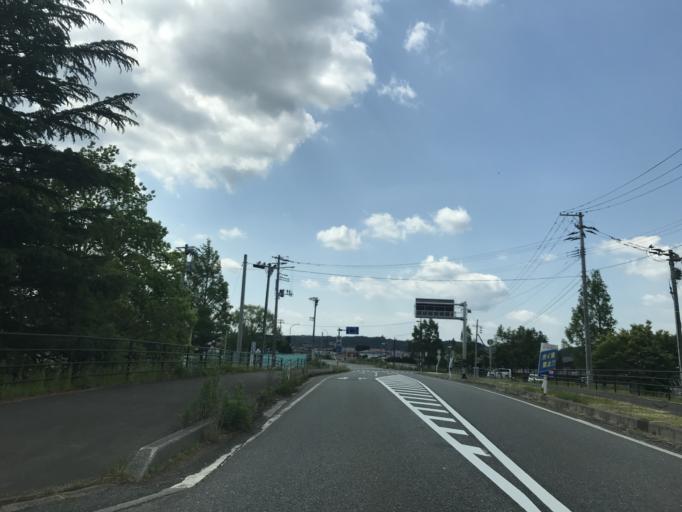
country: JP
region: Miyagi
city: Furukawa
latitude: 38.7453
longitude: 140.9540
